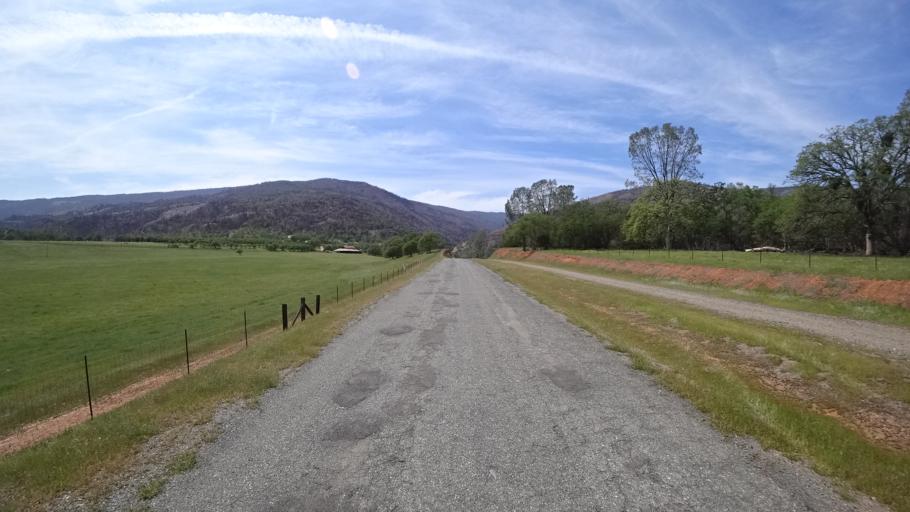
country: US
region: California
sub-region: Glenn County
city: Willows
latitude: 39.5759
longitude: -122.6095
